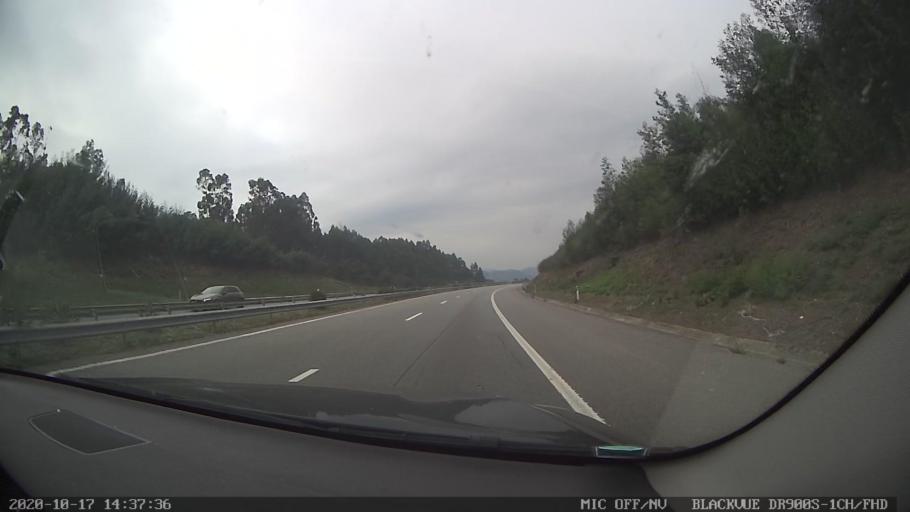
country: PT
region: Braga
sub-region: Vila Nova de Famalicao
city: Joane
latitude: 41.4830
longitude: -8.4022
